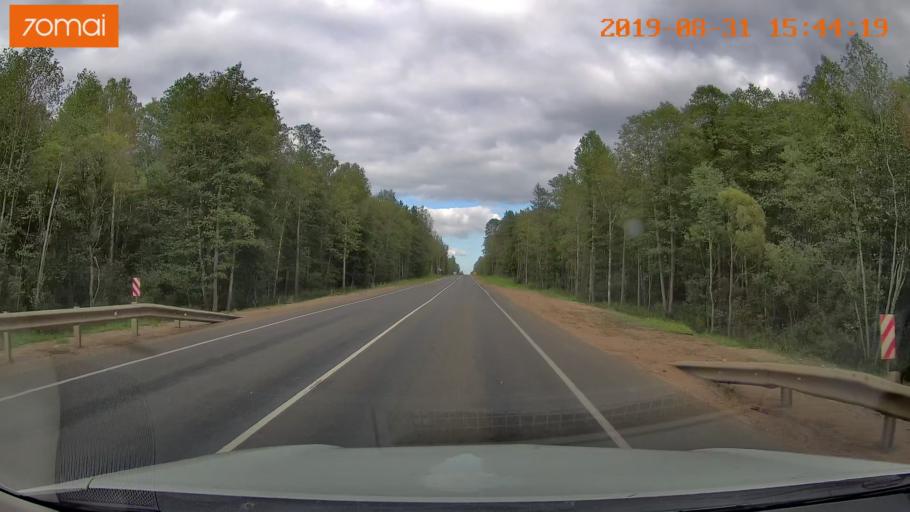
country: RU
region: Kaluga
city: Mosal'sk
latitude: 54.6583
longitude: 34.9302
